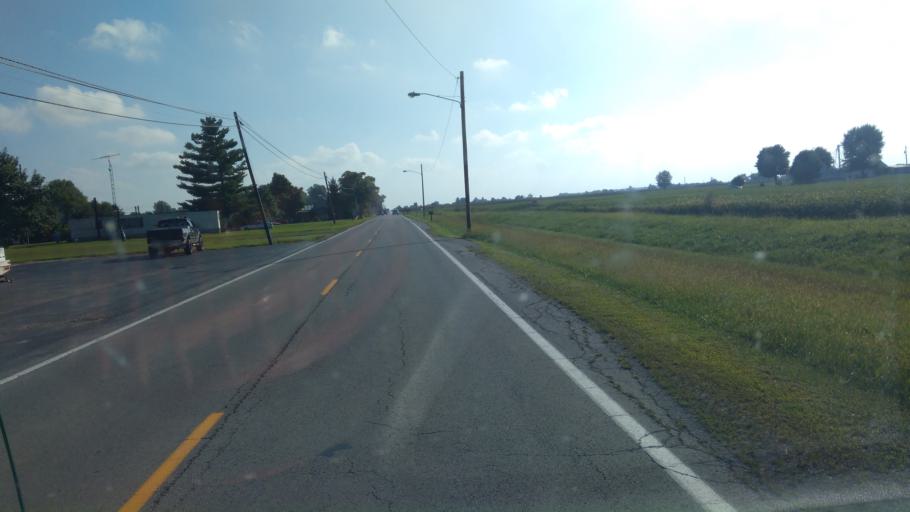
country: US
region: Ohio
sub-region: Hardin County
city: Forest
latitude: 40.7974
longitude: -83.5152
